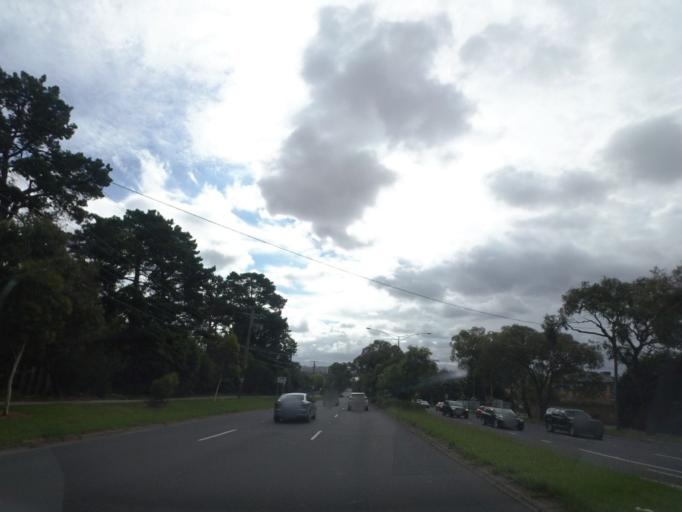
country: AU
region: Victoria
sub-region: Maroondah
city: Heathmont
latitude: -37.8324
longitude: 145.2371
